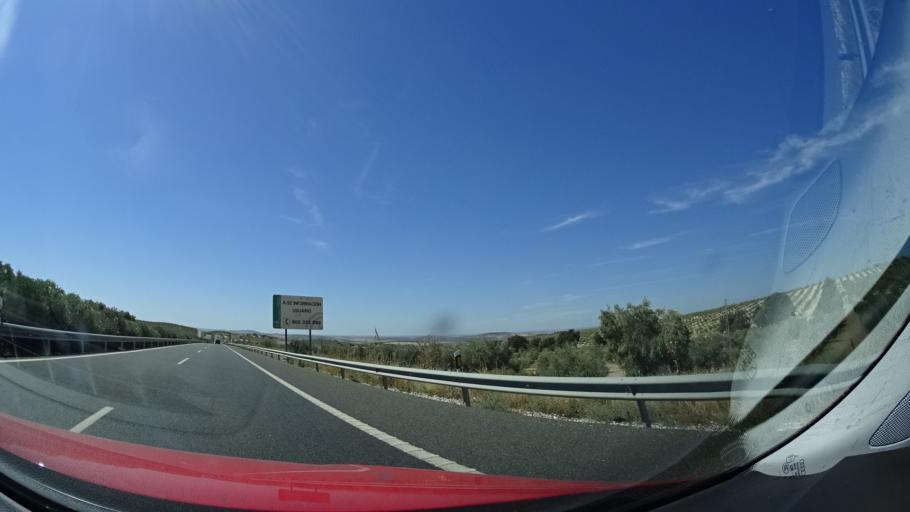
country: ES
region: Andalusia
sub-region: Provincia de Sevilla
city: Gilena
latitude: 37.2784
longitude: -4.9307
